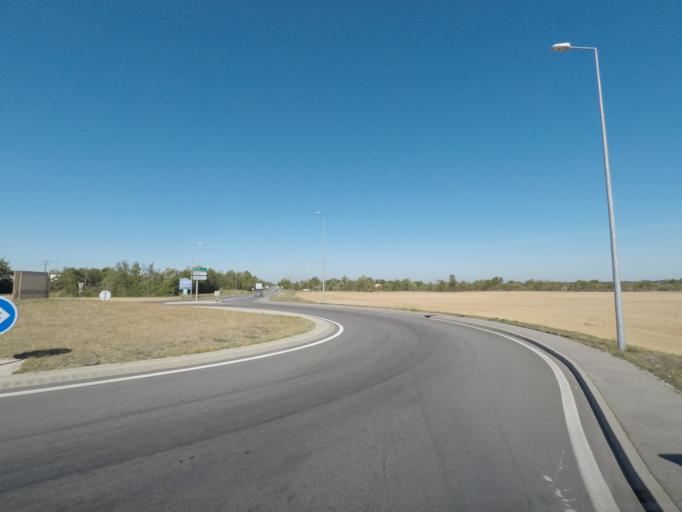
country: FR
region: Rhone-Alpes
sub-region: Departement de l'Ain
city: Attignat
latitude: 46.2594
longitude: 5.1769
